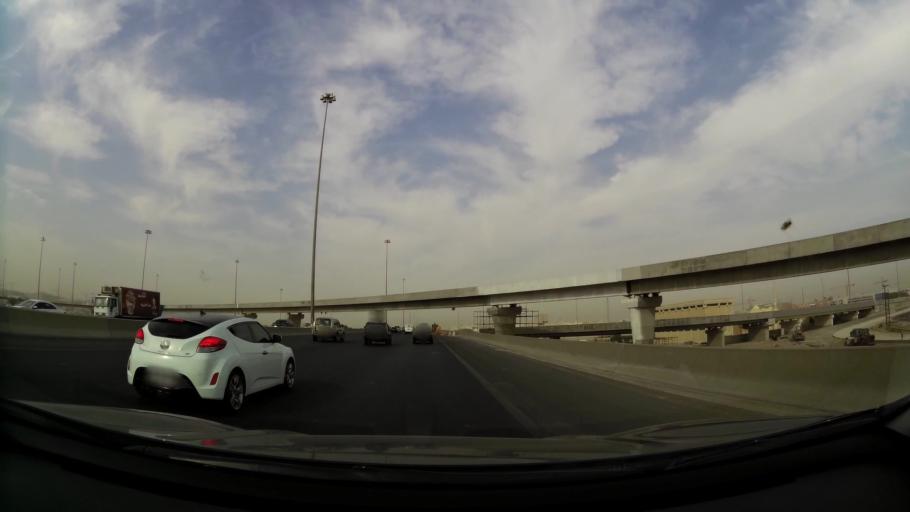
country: KW
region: Al Asimah
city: Ar Rabiyah
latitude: 29.2675
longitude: 47.9098
